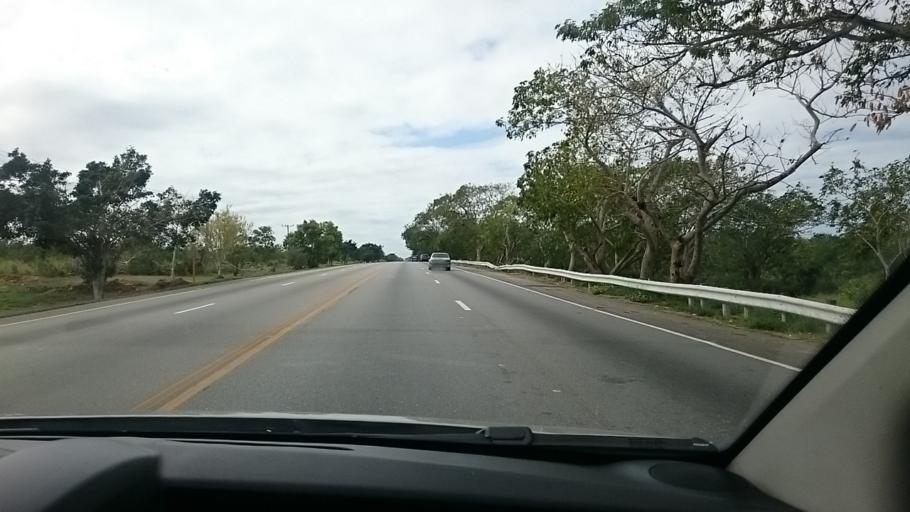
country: CU
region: La Habana
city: Alamar
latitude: 23.1649
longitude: -82.2603
